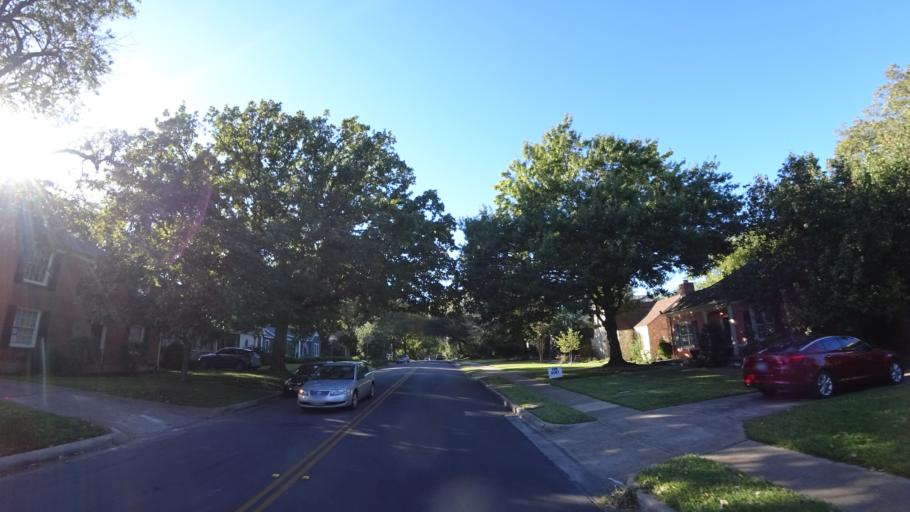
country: US
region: Texas
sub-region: Travis County
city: Austin
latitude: 30.3006
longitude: -97.7526
